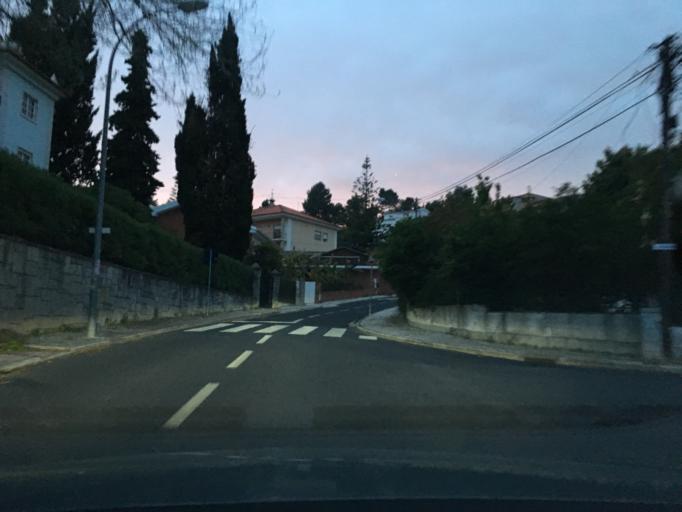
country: PT
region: Lisbon
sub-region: Oeiras
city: Terrugem
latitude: 38.7031
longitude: -9.2789
